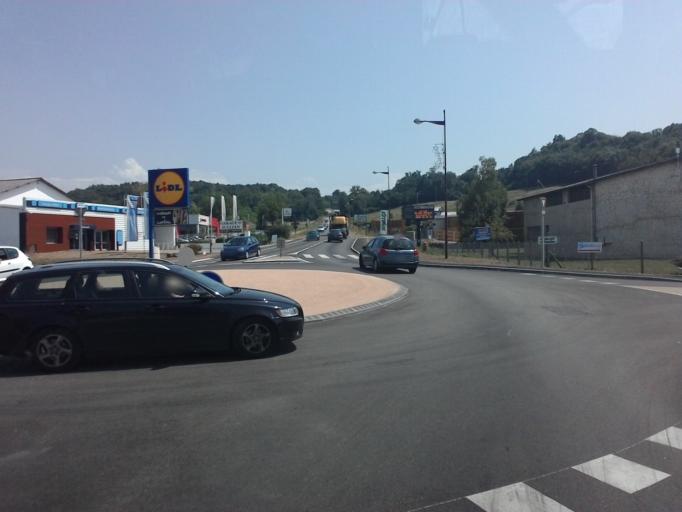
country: FR
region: Rhone-Alpes
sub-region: Departement de l'Isere
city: Les Abrets
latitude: 45.5270
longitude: 5.5921
